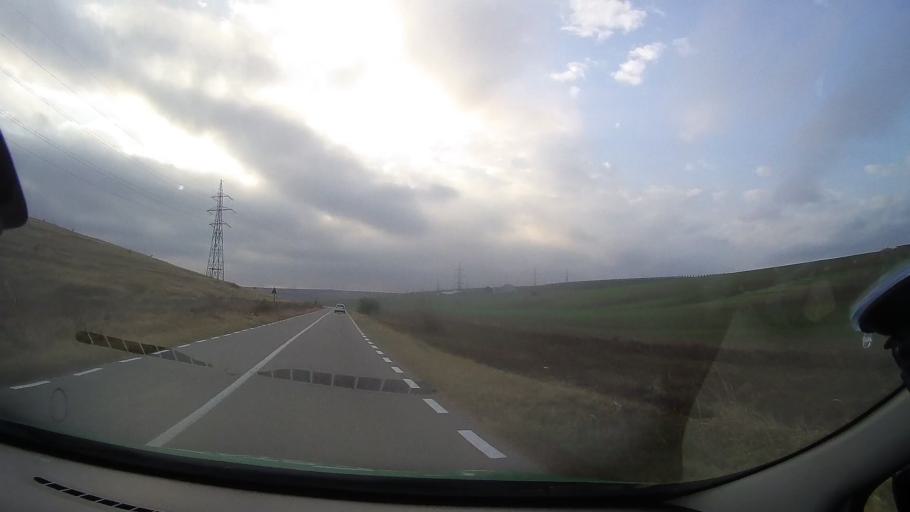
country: RO
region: Constanta
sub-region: Comuna Pestera
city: Pestera
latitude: 44.2016
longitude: 28.1427
